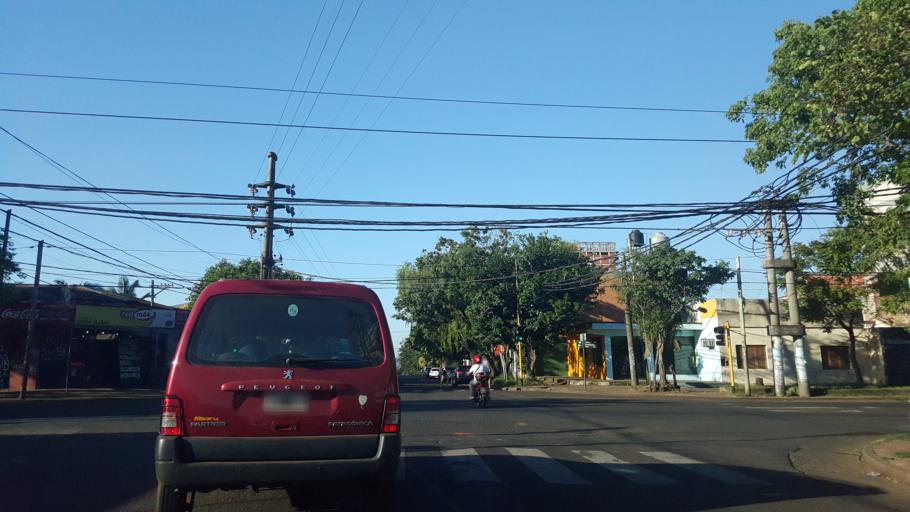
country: AR
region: Misiones
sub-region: Departamento de Capital
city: Posadas
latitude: -27.3671
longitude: -55.9051
